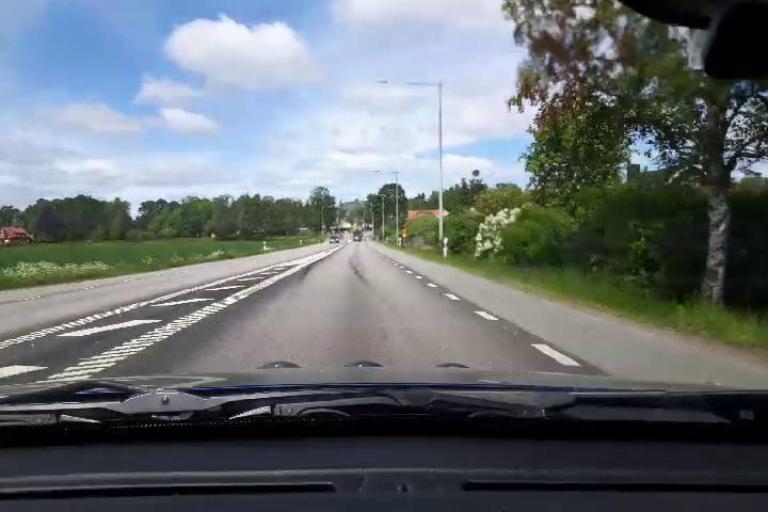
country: SE
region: Uppsala
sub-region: Osthammars Kommun
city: Bjorklinge
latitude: 60.0236
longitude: 17.5541
